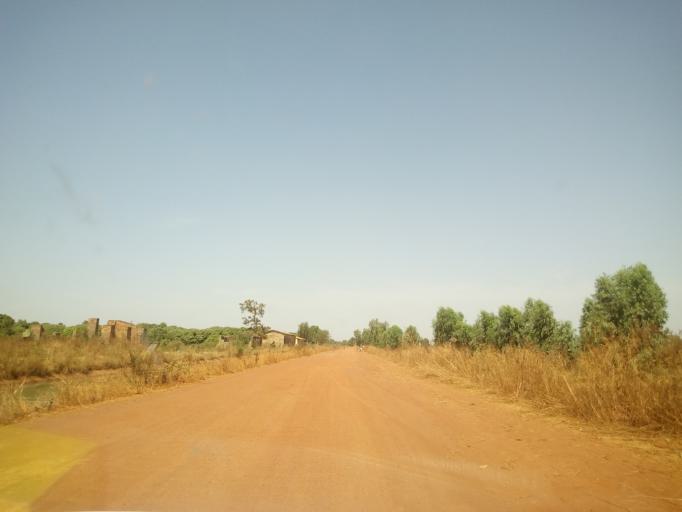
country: ML
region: Bamako
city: Bamako
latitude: 12.6212
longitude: -7.7769
